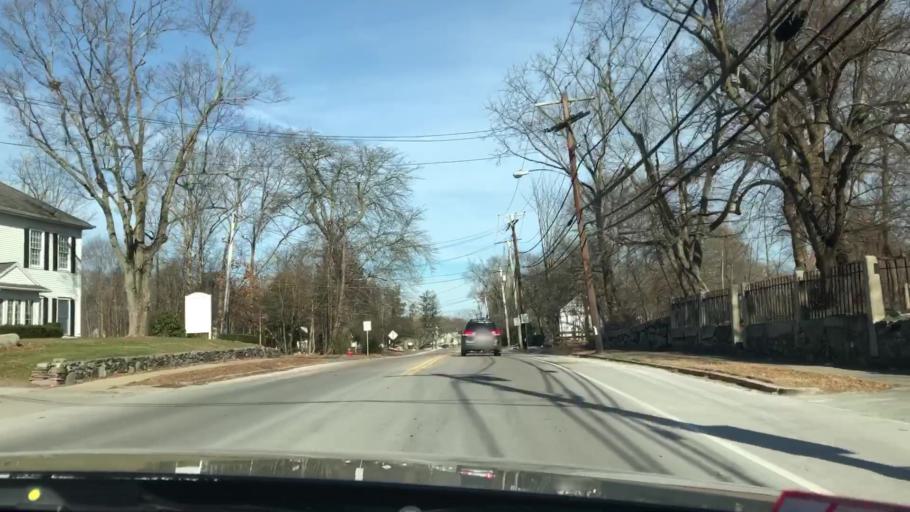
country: US
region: Massachusetts
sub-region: Norfolk County
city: Walpole
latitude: 42.1497
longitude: -71.2502
